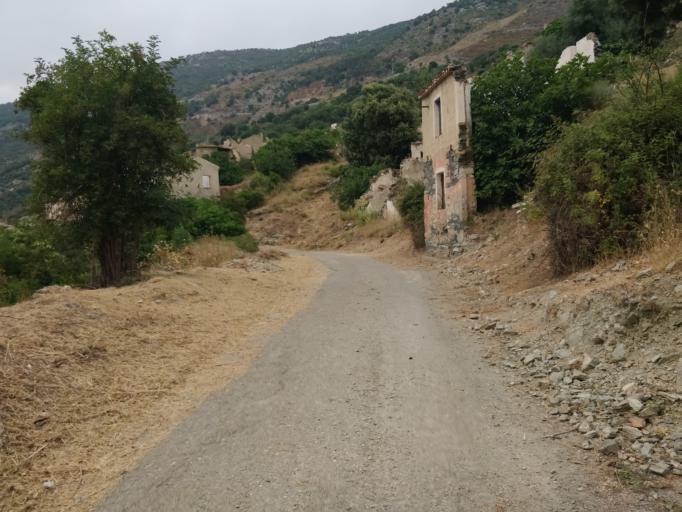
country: IT
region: Sardinia
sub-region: Provincia di Ogliastra
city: Gairo Sant'Elena
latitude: 39.8454
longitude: 9.5001
